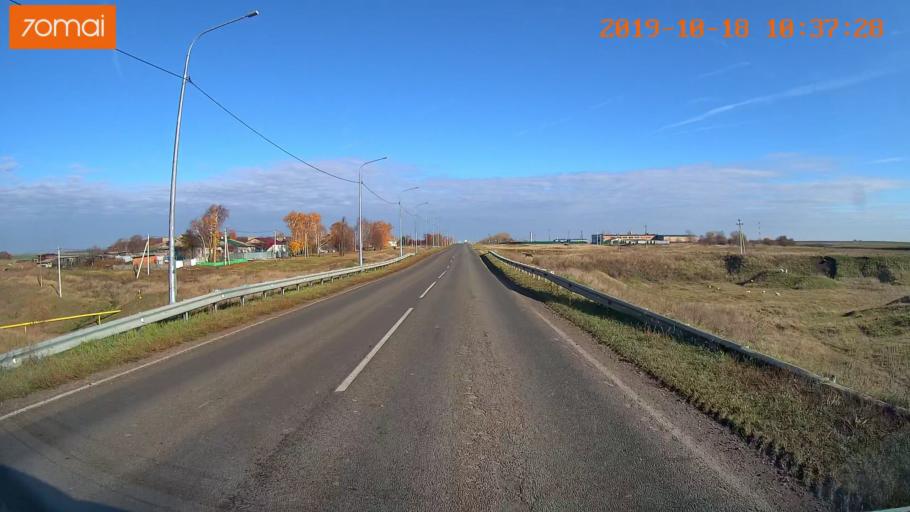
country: RU
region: Tula
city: Kurkino
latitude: 53.5625
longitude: 38.6323
